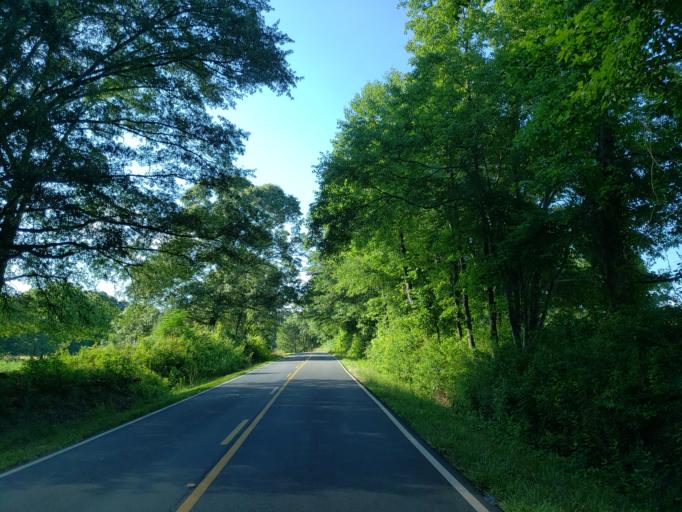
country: US
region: Georgia
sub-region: Carroll County
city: Mount Zion
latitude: 33.6502
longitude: -85.1109
